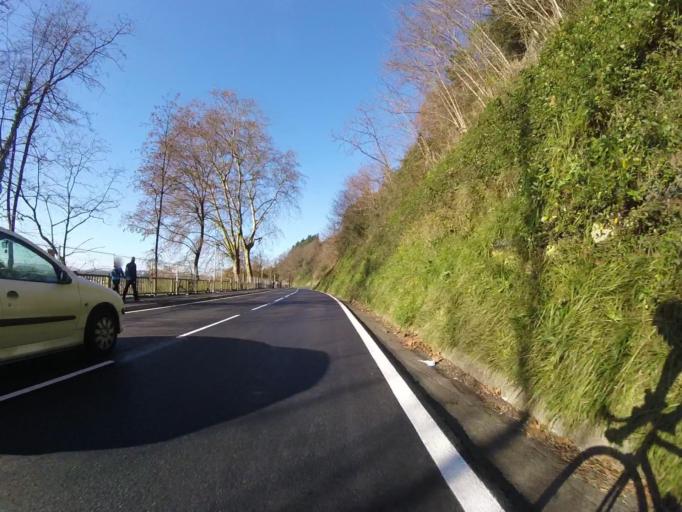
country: ES
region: Basque Country
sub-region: Provincia de Guipuzcoa
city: Lezo
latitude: 43.3245
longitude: -1.9023
